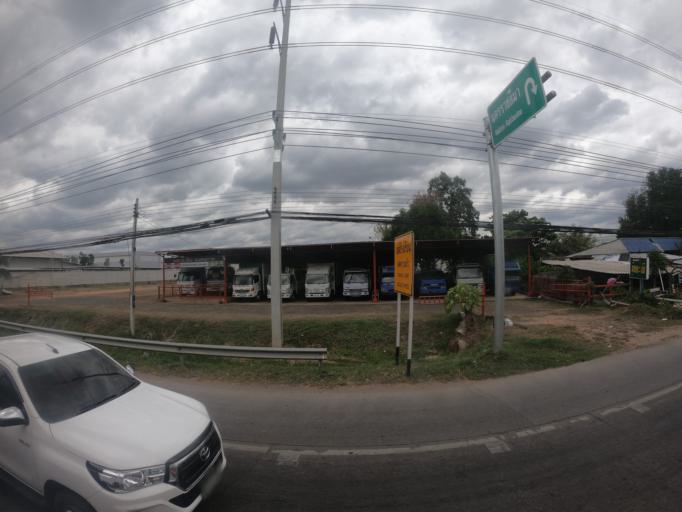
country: TH
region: Nakhon Ratchasima
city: Nakhon Ratchasima
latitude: 14.9274
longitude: 102.1406
